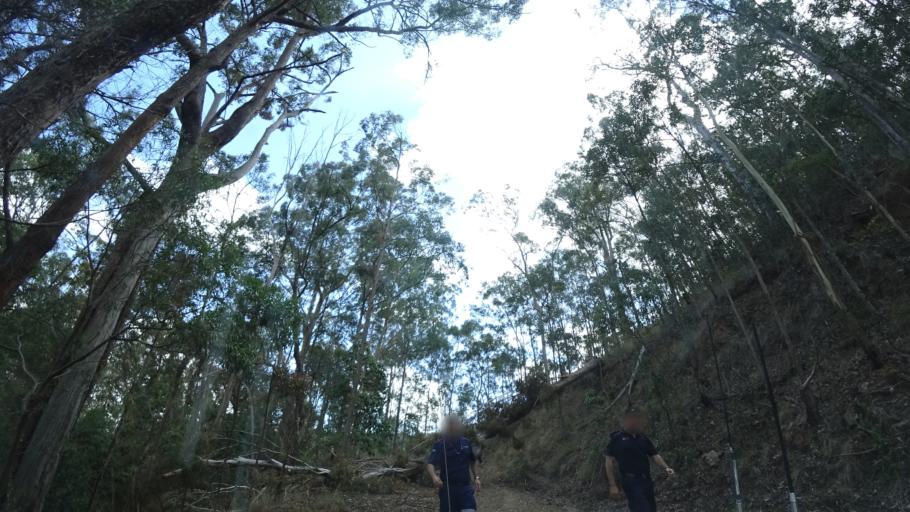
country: AU
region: Queensland
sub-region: Moreton Bay
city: Highvale
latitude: -27.3445
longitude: 152.7245
